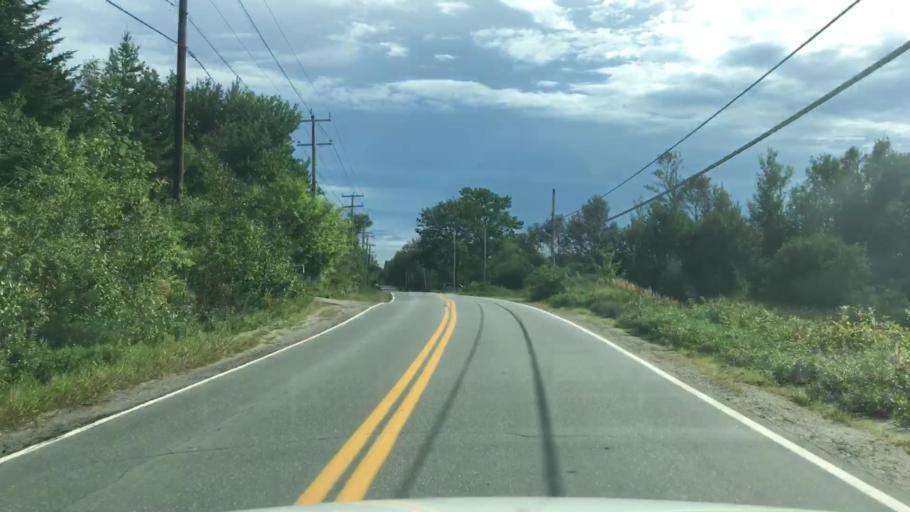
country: US
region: Maine
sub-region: Hancock County
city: Ellsworth
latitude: 44.4997
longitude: -68.4204
